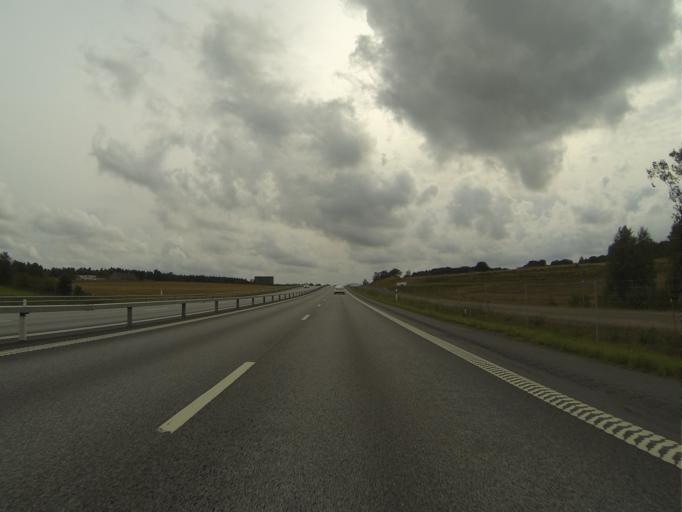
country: SE
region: Skane
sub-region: Horby Kommun
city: Hoerby
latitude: 55.8710
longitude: 13.7026
